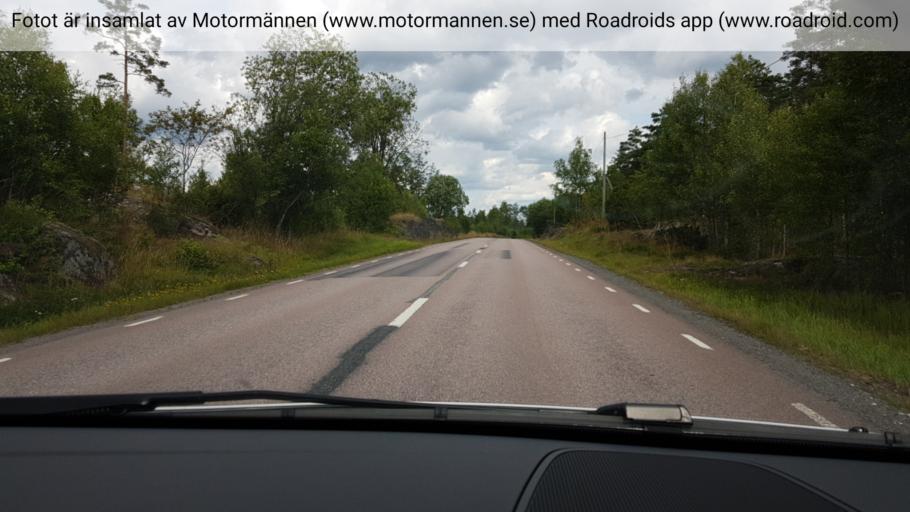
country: SE
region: Stockholm
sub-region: Norrtalje Kommun
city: Nykvarn
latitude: 59.8328
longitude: 18.0473
